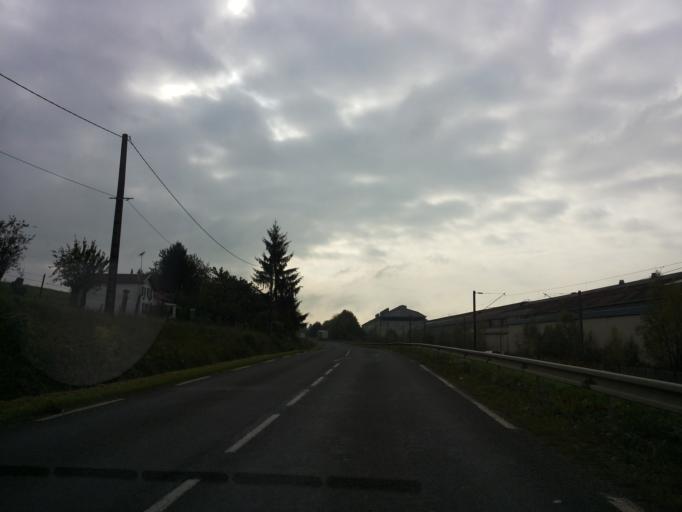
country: FR
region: Champagne-Ardenne
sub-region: Departement des Ardennes
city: Blagny
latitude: 49.6184
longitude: 5.1926
